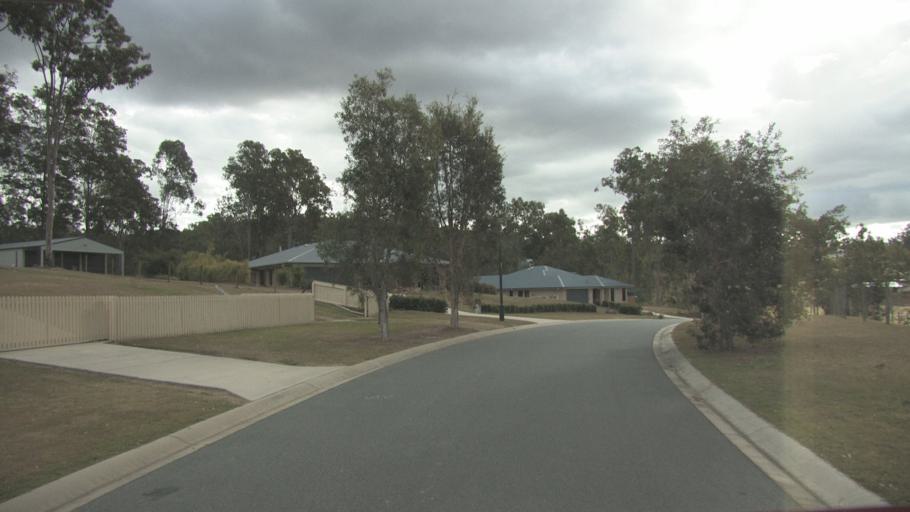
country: AU
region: Queensland
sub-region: Logan
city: Cedar Vale
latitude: -27.8655
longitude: 153.0742
